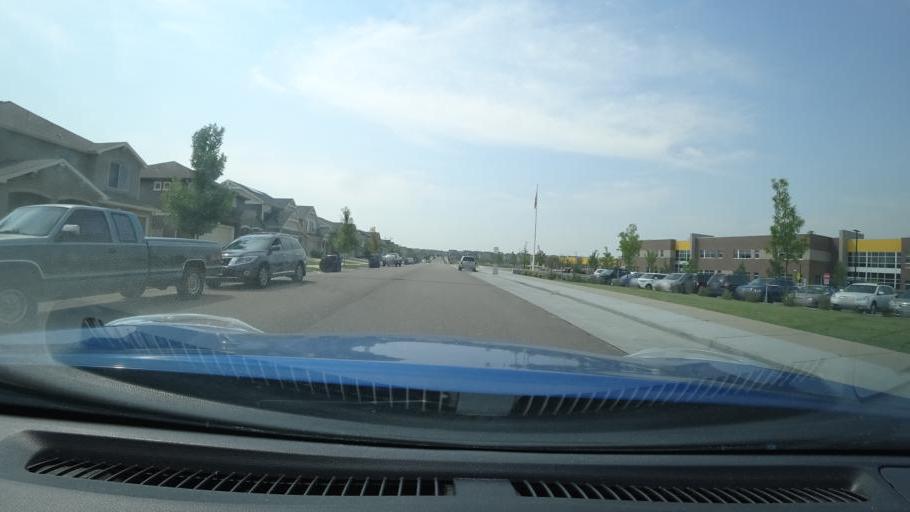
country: US
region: Colorado
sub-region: Adams County
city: Aurora
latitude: 39.7813
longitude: -104.7777
